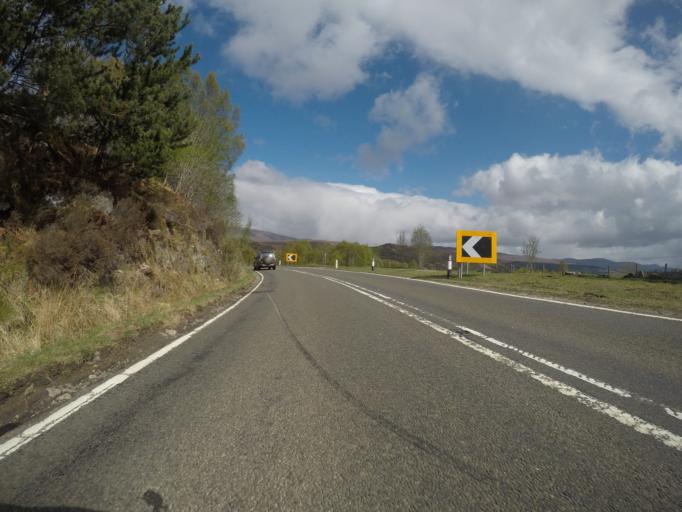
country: GB
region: Scotland
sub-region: Highland
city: Spean Bridge
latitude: 57.1413
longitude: -4.9520
